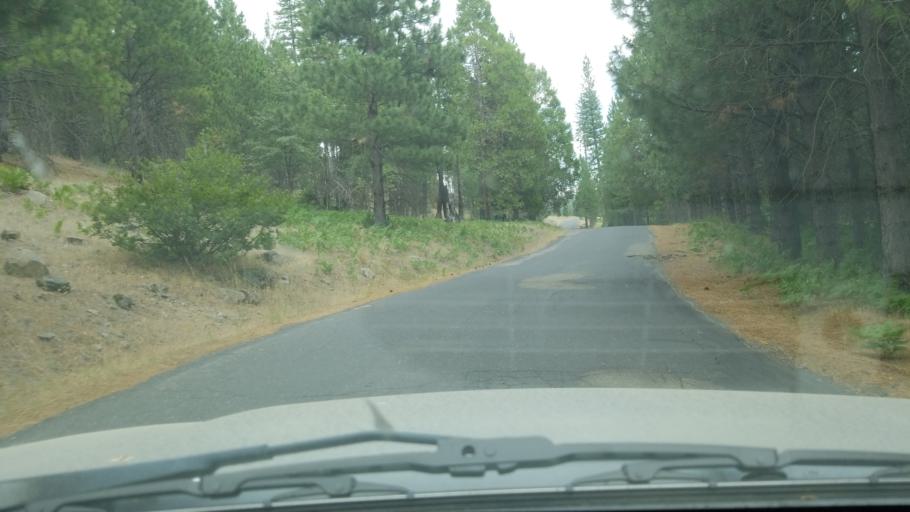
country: US
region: California
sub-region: Mariposa County
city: Yosemite Valley
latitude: 37.8464
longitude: -119.8556
